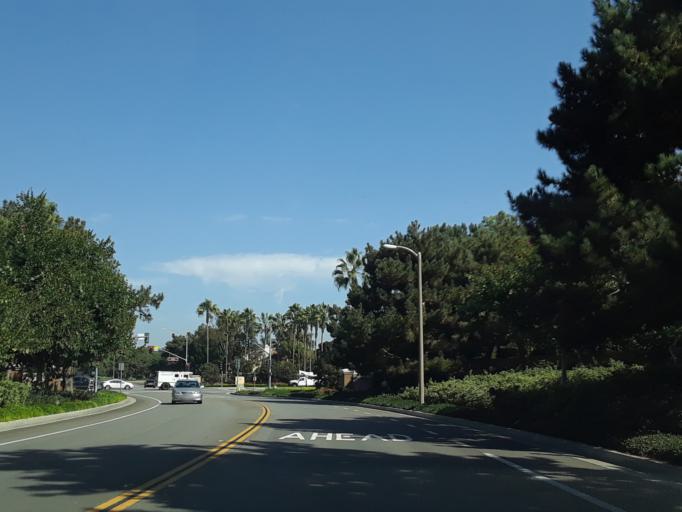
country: US
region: California
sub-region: Orange County
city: Irvine
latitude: 33.6776
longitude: -117.8212
